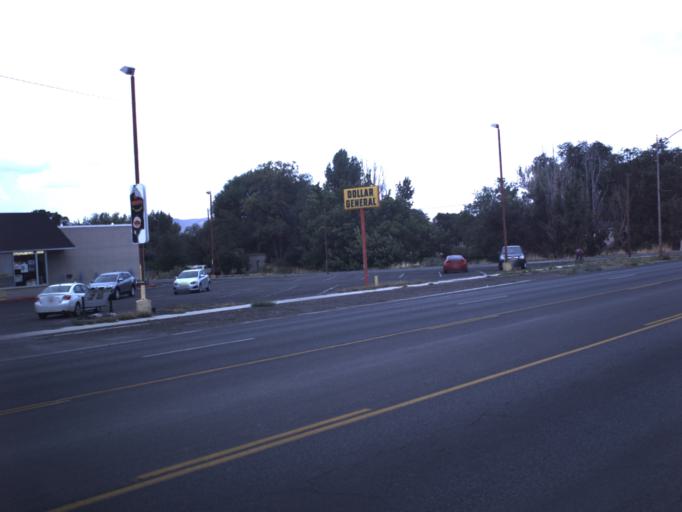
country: US
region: Utah
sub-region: Juab County
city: Nephi
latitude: 39.7136
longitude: -111.8361
